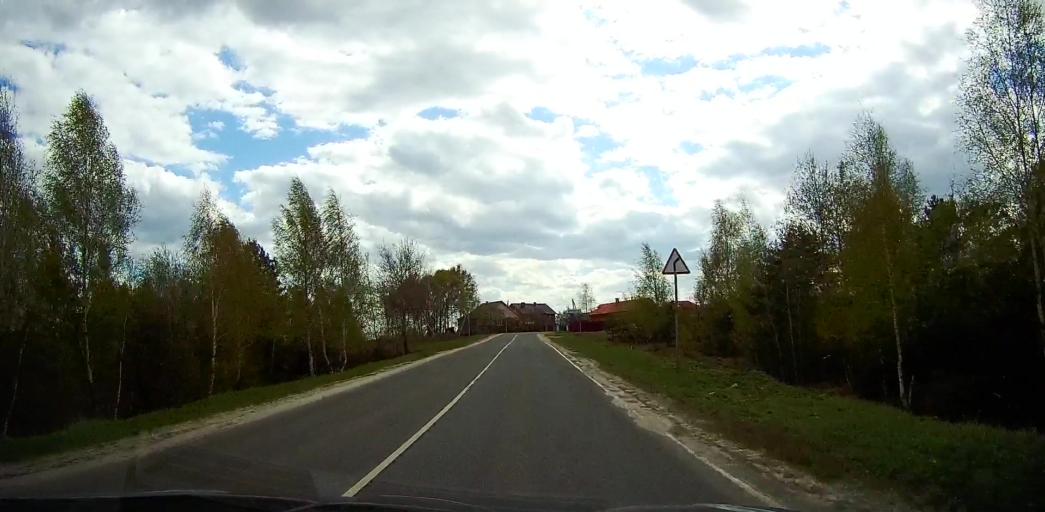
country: RU
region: Moskovskaya
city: Davydovo
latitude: 55.6325
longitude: 38.7452
